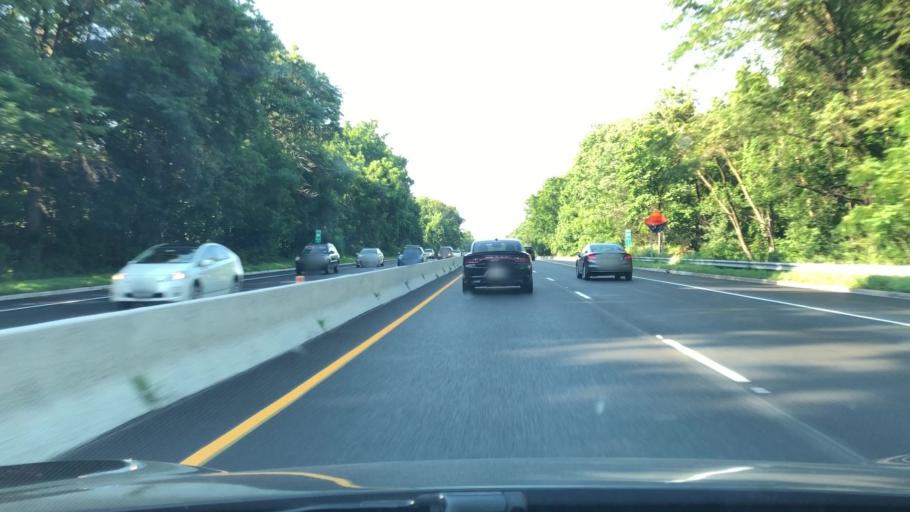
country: US
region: New Jersey
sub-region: Mercer County
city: Mercerville
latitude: 40.2553
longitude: -74.7193
